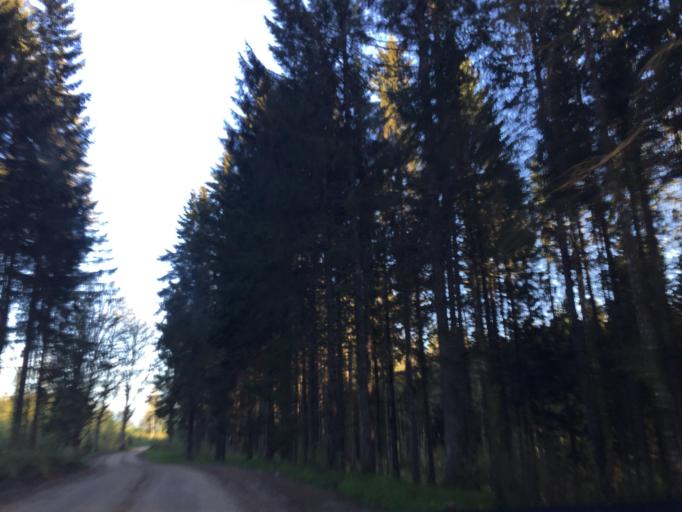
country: LV
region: Vecpiebalga
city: Vecpiebalga
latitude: 56.8502
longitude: 25.9564
